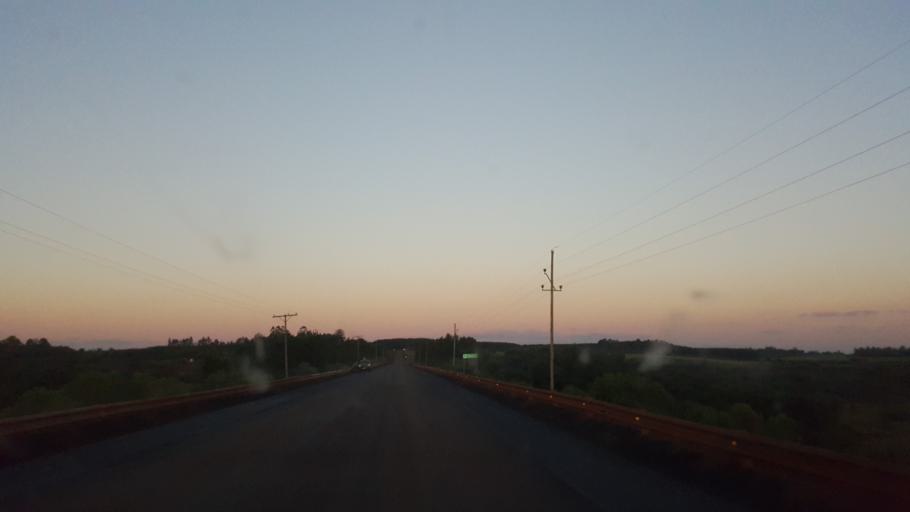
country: AR
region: Corrientes
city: Garruchos
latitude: -28.2332
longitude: -55.8139
